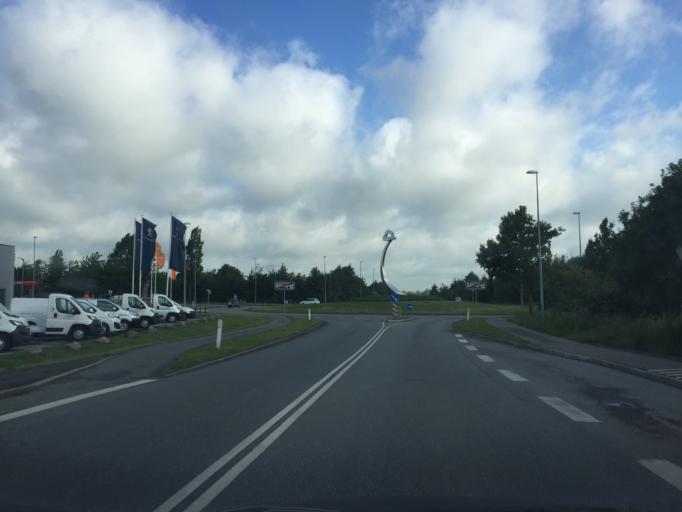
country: DK
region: Zealand
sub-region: Slagelse Kommune
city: Slagelse
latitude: 55.4145
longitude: 11.4011
